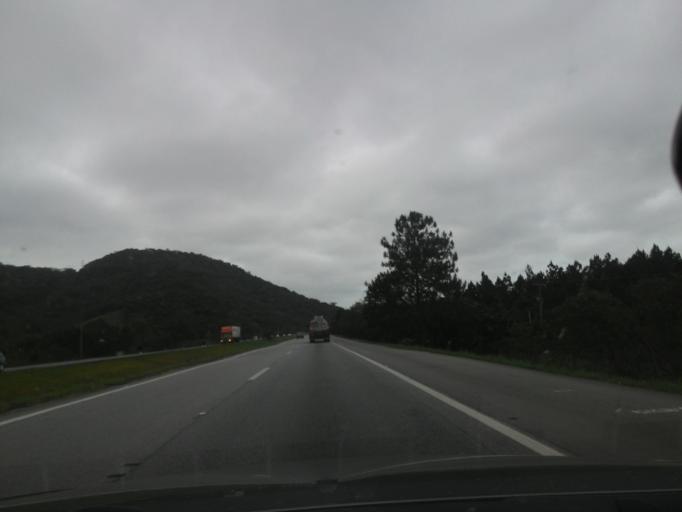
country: BR
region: Santa Catarina
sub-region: Florianopolis
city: Pantano do Sul
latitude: -27.8596
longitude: -48.6444
